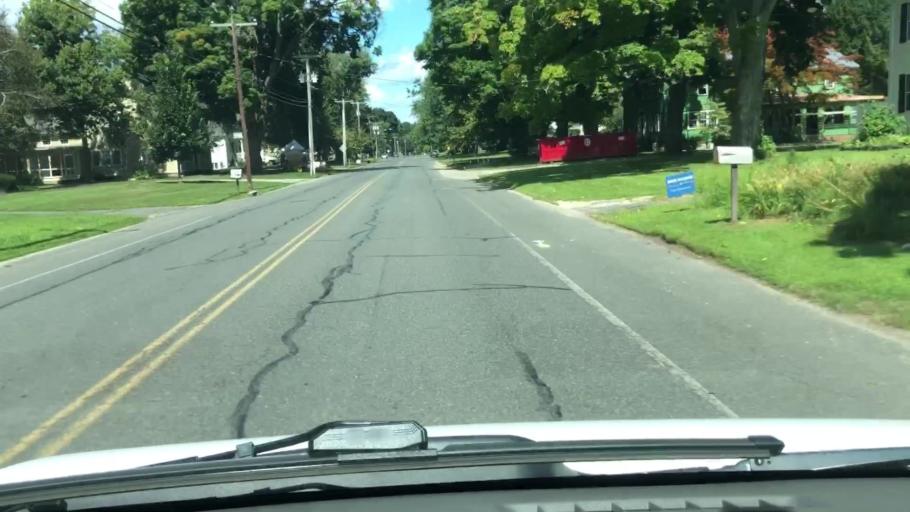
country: US
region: Massachusetts
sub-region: Hampshire County
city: Hatfield
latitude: 42.3705
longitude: -72.5966
